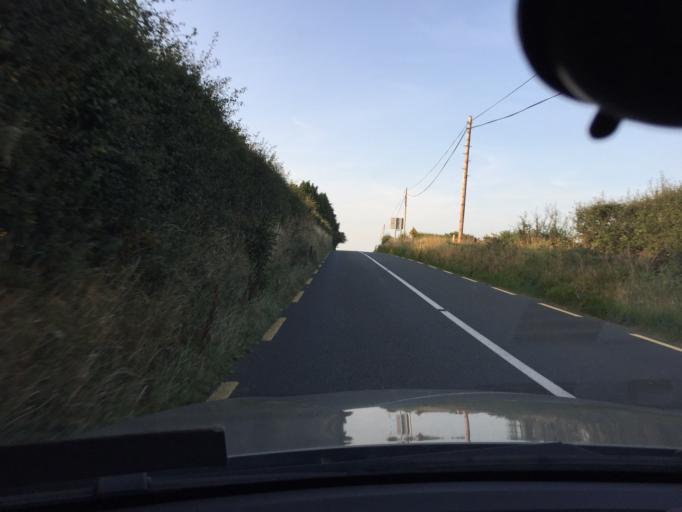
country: IE
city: Newtownmountkennedy
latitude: 53.0882
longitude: -6.2084
